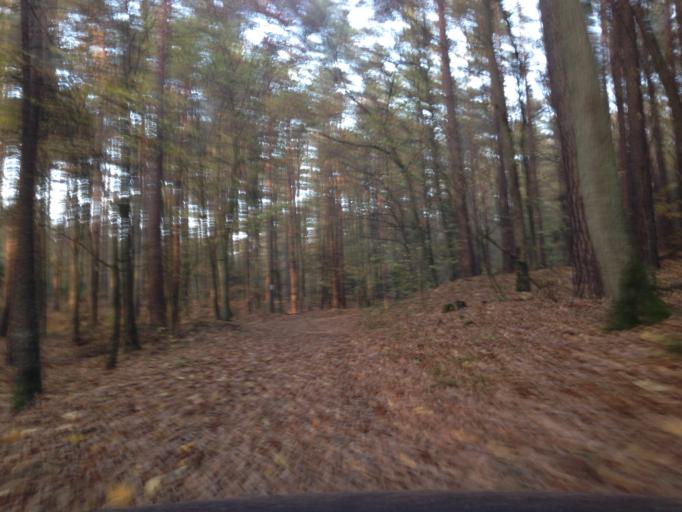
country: PL
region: Kujawsko-Pomorskie
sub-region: Powiat brodnicki
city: Gorzno
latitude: 53.2490
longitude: 19.7268
